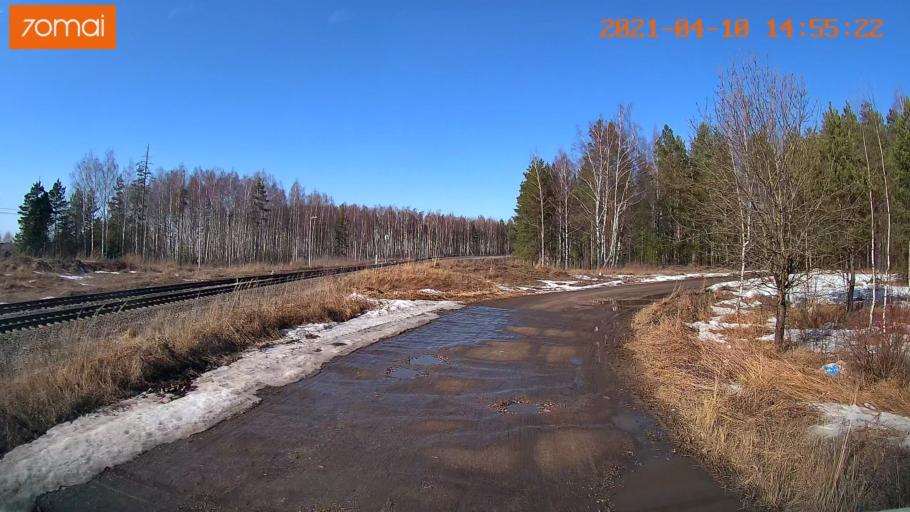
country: RU
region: Ivanovo
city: Kokhma
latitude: 56.9892
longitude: 41.0572
